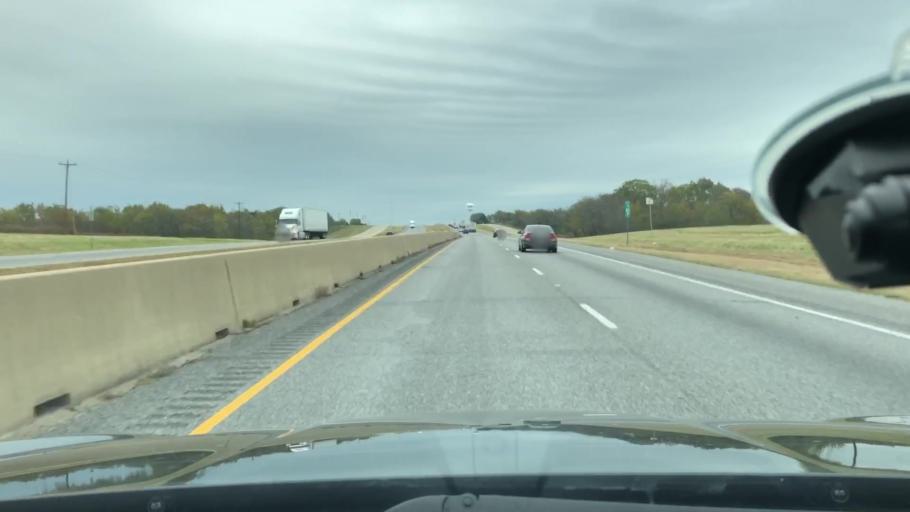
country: US
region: Texas
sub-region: Hunt County
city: Commerce
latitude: 33.1304
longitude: -95.8983
